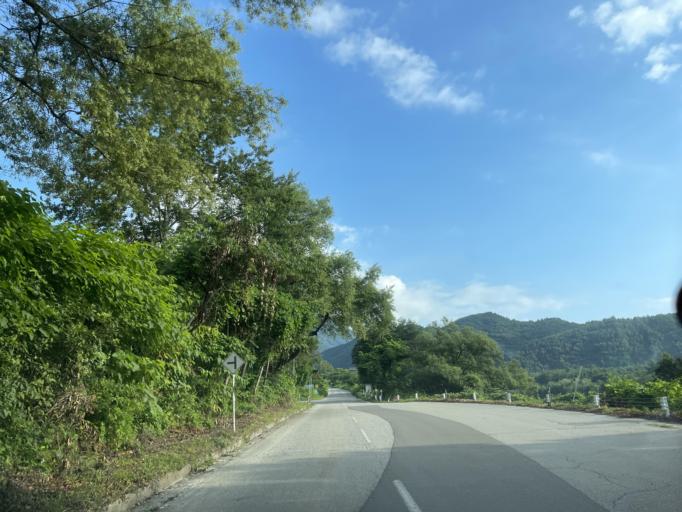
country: JP
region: Nagano
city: Omachi
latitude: 36.5257
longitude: 137.7908
